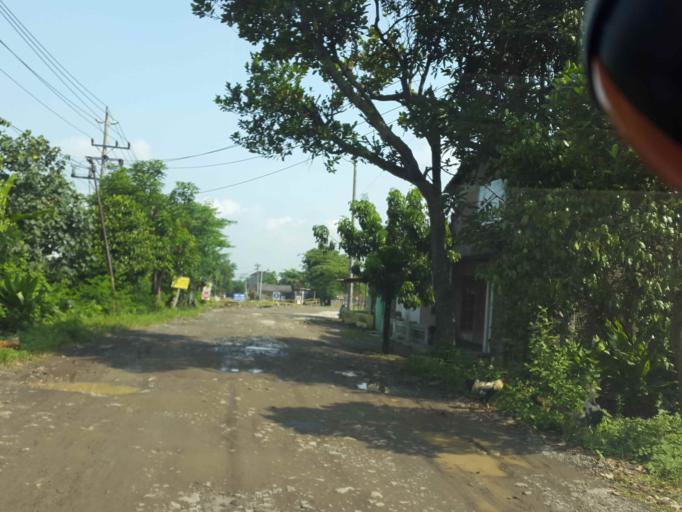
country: ID
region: Central Java
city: Sragen
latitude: -7.4508
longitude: 110.9524
